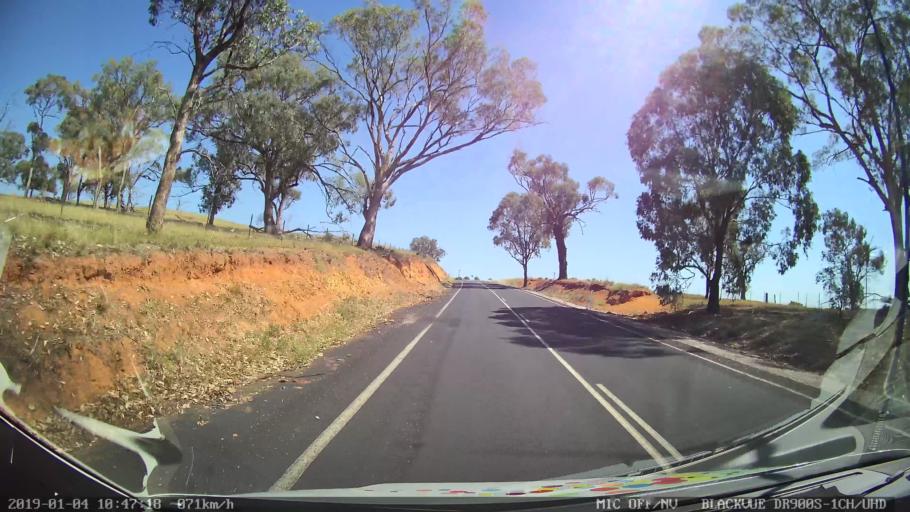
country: AU
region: New South Wales
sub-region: Cabonne
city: Molong
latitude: -33.2714
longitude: 148.7200
